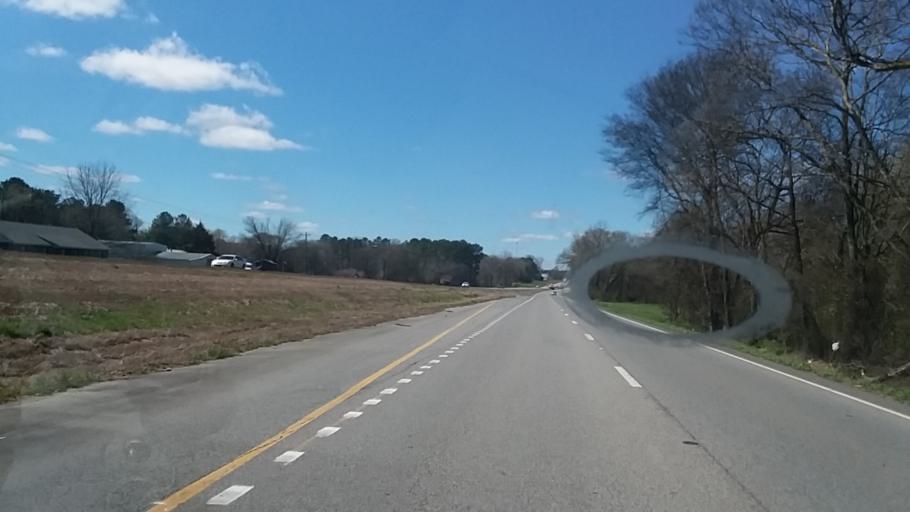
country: US
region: Alabama
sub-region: Colbert County
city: Tuscumbia
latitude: 34.7184
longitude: -87.7942
